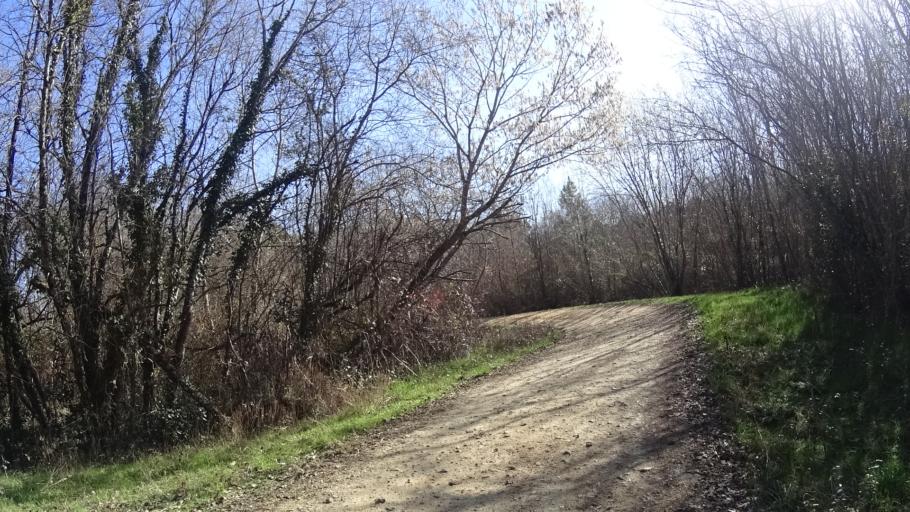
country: FR
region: Aquitaine
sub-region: Departement de la Dordogne
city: Montpon-Menesterol
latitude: 45.1022
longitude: 0.1952
